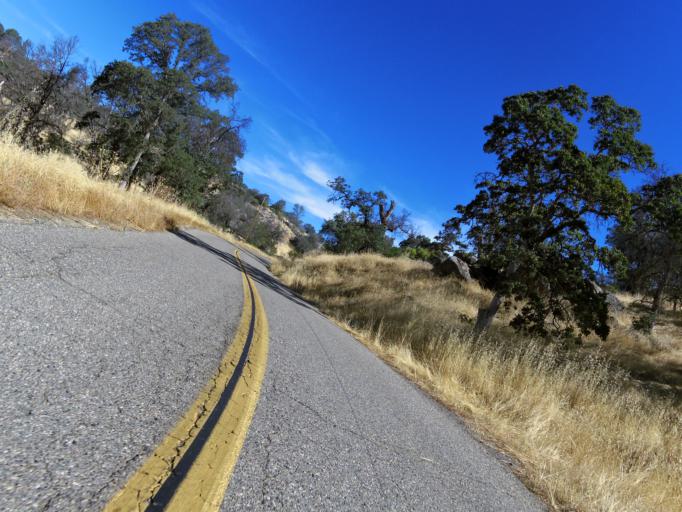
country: US
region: California
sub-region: Mariposa County
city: Mariposa
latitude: 37.2878
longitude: -119.9767
